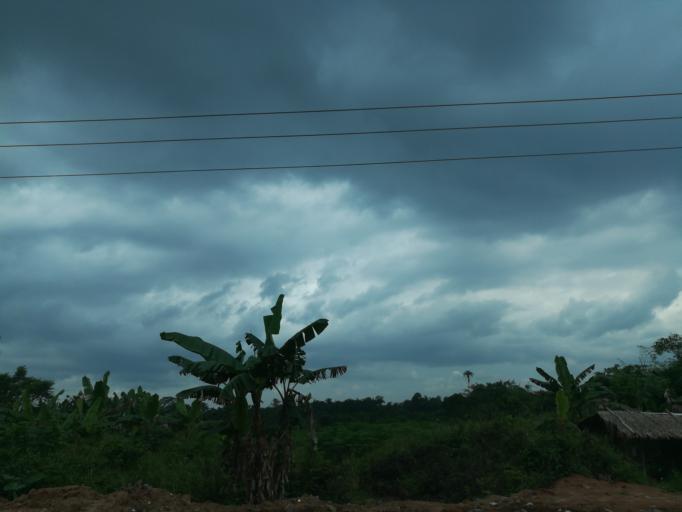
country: NG
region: Lagos
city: Ejirin
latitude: 6.6449
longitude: 3.8479
